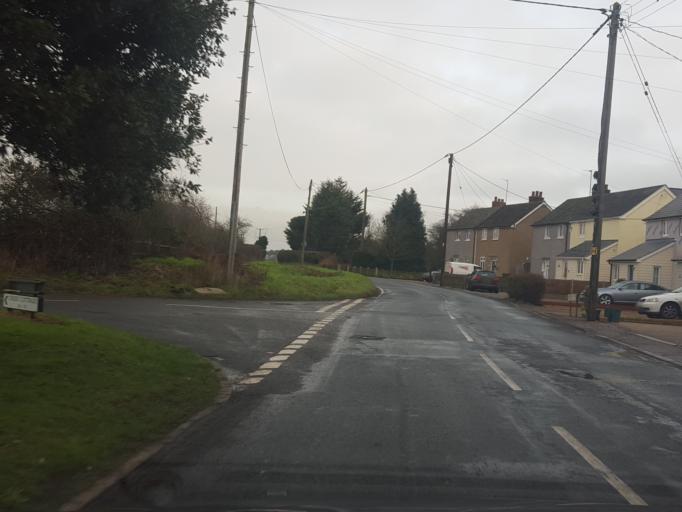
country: GB
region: England
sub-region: Essex
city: Great Horkesley
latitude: 51.9558
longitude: 0.9218
